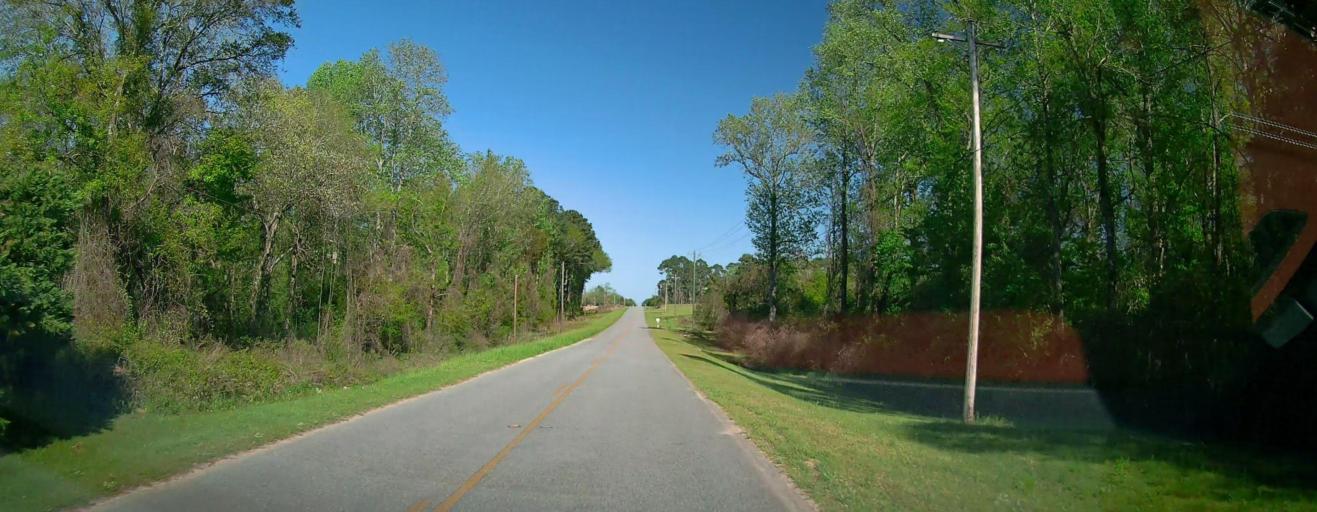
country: US
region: Georgia
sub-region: Pulaski County
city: Hawkinsville
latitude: 32.2478
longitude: -83.4918
